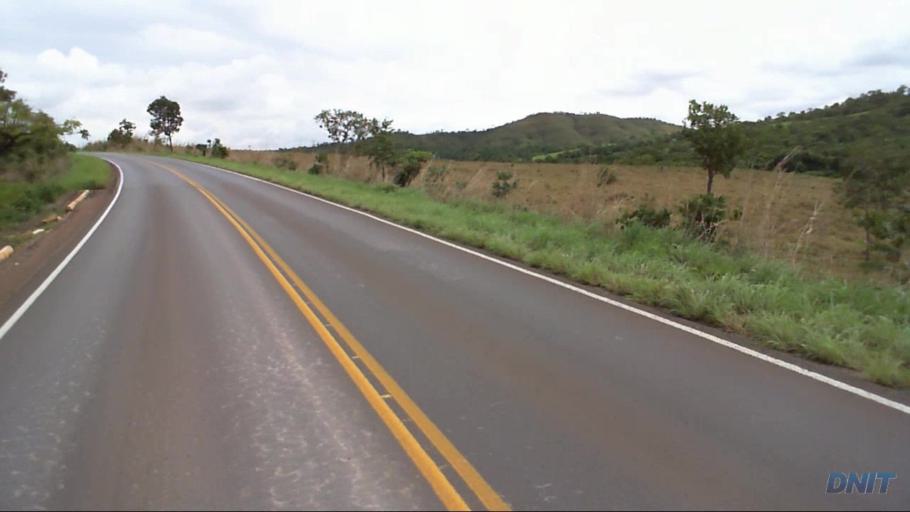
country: BR
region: Goias
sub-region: Padre Bernardo
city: Padre Bernardo
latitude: -15.4339
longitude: -48.1929
